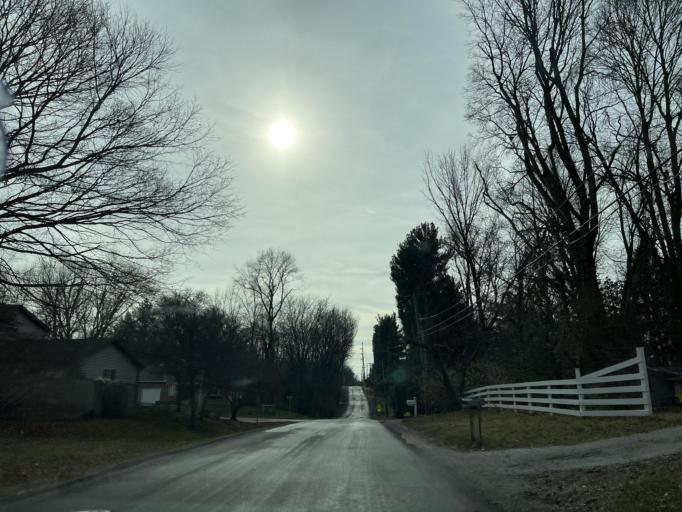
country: US
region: Illinois
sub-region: Sangamon County
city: Leland Grove
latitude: 39.7861
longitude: -89.7339
